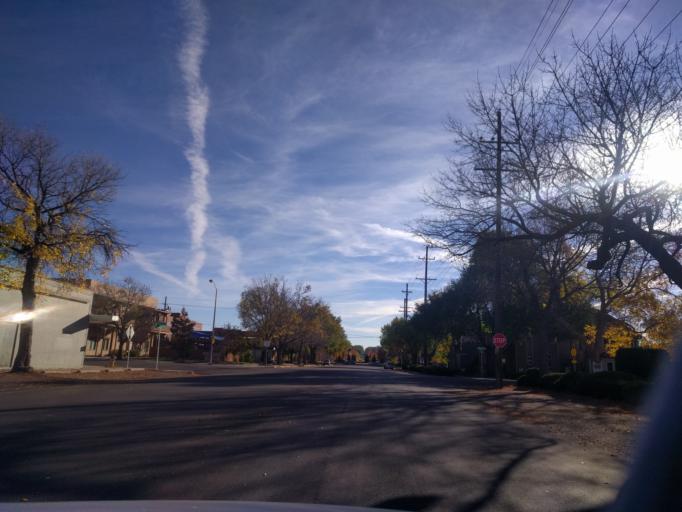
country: US
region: Colorado
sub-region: El Paso County
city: Colorado Springs
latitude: 38.8231
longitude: -104.8247
